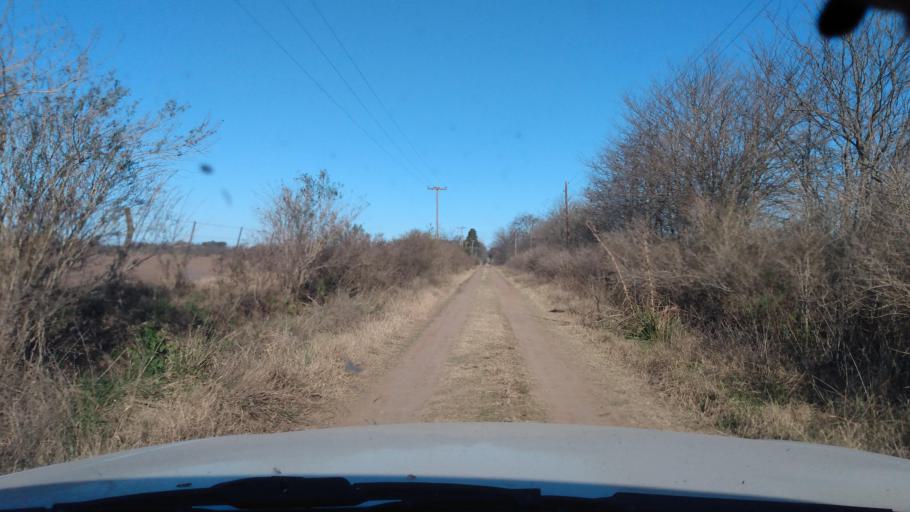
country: AR
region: Buenos Aires
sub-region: Partido de Mercedes
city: Mercedes
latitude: -34.6380
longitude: -59.3743
